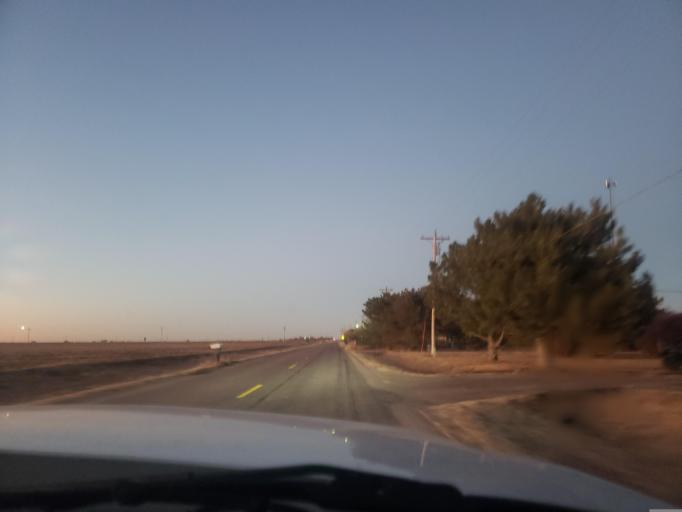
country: US
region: Kansas
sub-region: Finney County
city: Garden City
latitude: 37.9978
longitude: -100.8749
